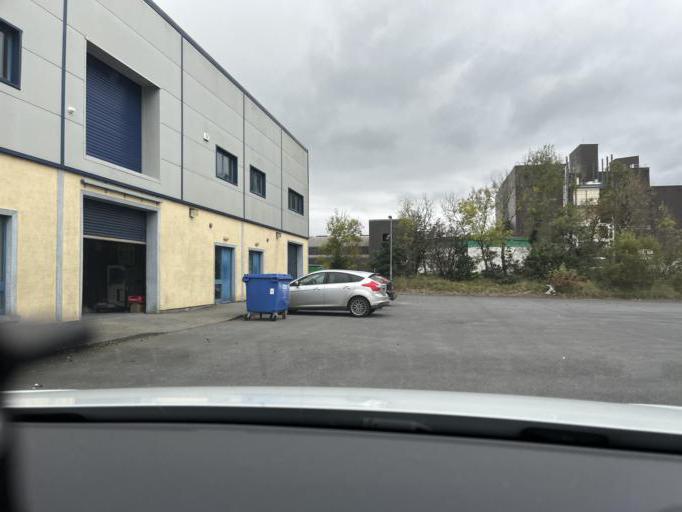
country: IE
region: Connaught
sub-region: Roscommon
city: Ballaghaderreen
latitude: 53.8973
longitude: -8.5730
